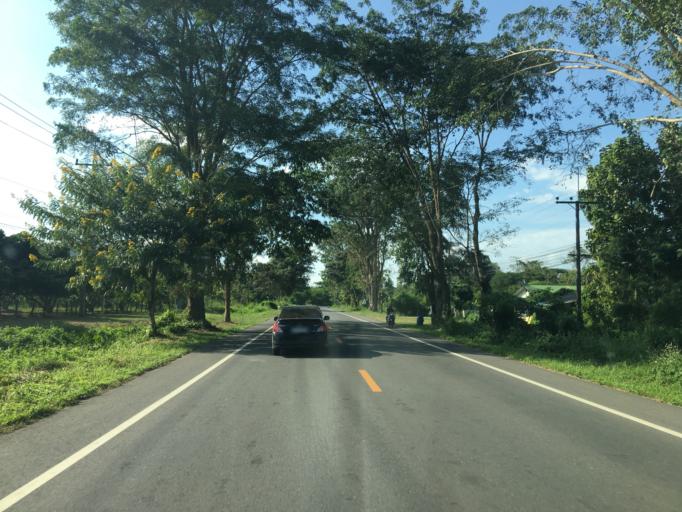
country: TH
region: Phayao
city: Chun
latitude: 19.3536
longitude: 100.1013
